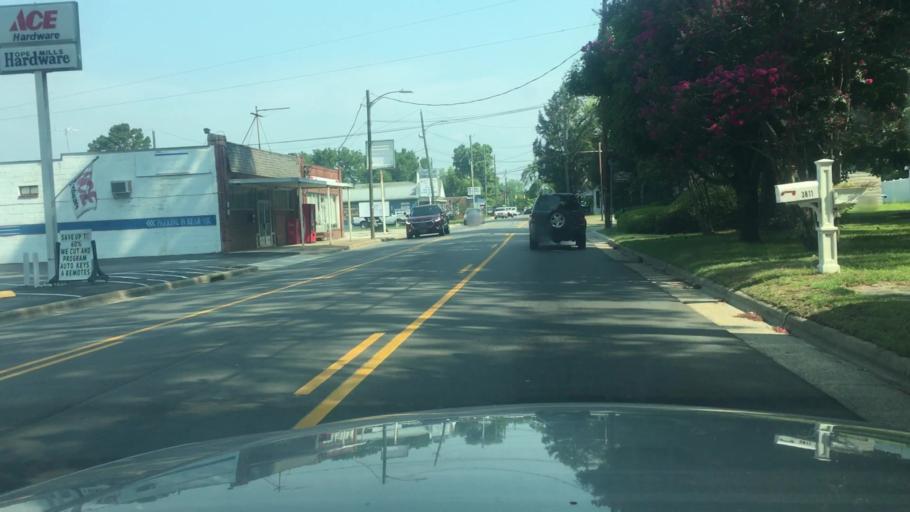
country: US
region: North Carolina
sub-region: Cumberland County
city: Hope Mills
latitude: 34.9696
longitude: -78.9452
